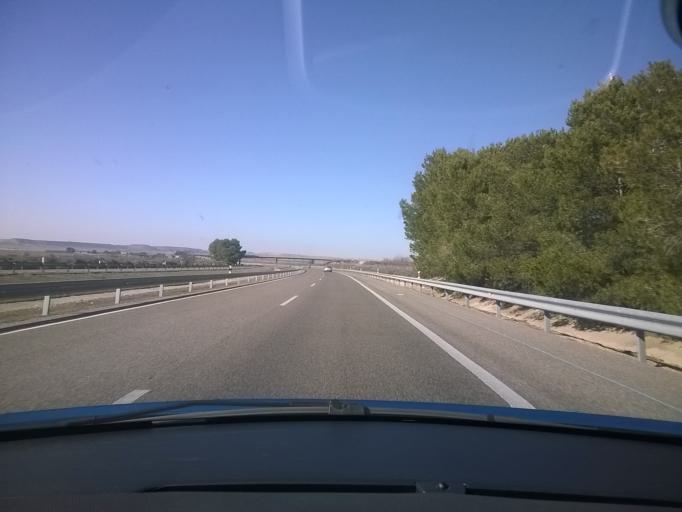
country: ES
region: Aragon
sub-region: Provincia de Huesca
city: Candasnos
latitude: 41.5189
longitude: 0.0797
